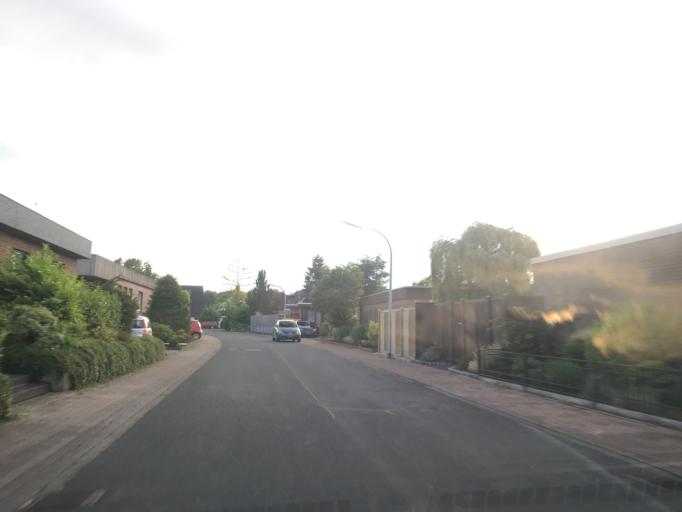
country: DE
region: North Rhine-Westphalia
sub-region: Regierungsbezirk Munster
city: Muenster
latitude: 51.9200
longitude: 7.5787
